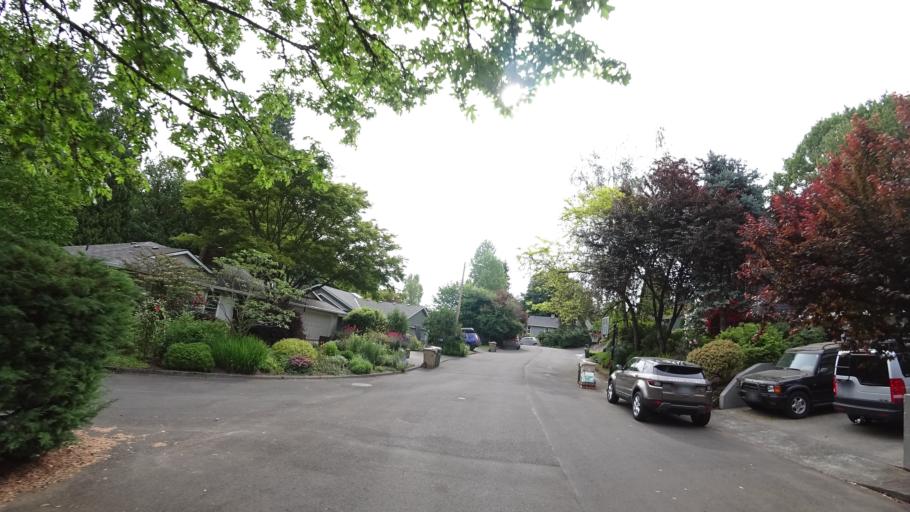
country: US
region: Oregon
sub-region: Clackamas County
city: Lake Oswego
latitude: 45.4315
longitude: -122.6841
